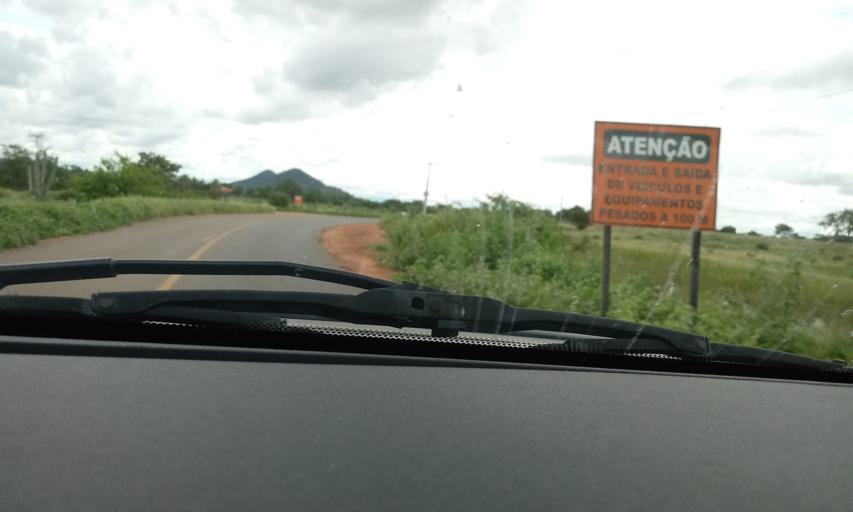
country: BR
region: Bahia
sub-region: Guanambi
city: Guanambi
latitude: -14.0959
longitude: -42.8724
